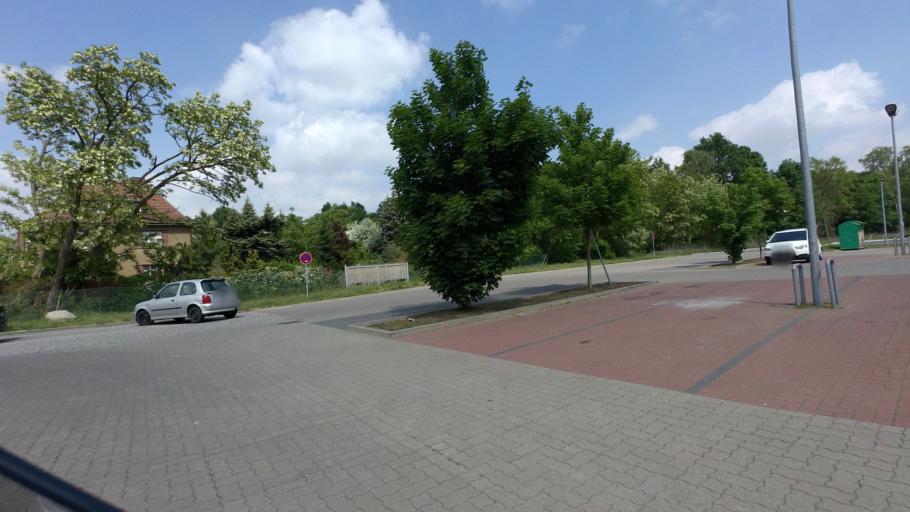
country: DE
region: Brandenburg
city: Cottbus
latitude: 51.7161
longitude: 14.3512
